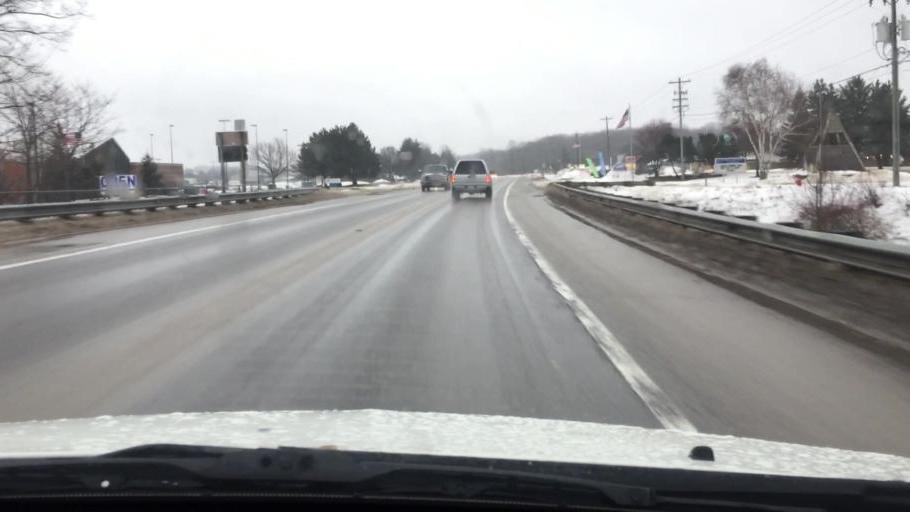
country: US
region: Michigan
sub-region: Charlevoix County
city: Charlevoix
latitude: 45.3007
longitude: -85.2571
